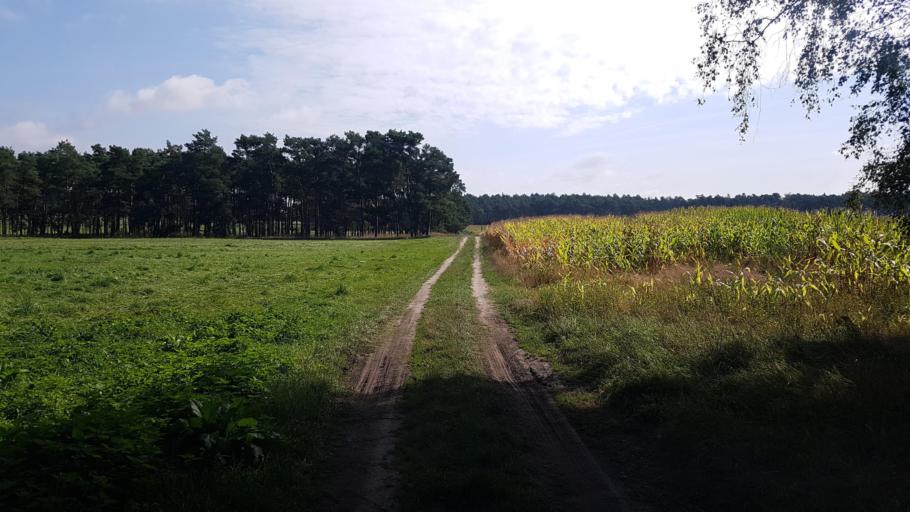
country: DE
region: Brandenburg
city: Hohenbucko
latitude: 51.7210
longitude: 13.4879
